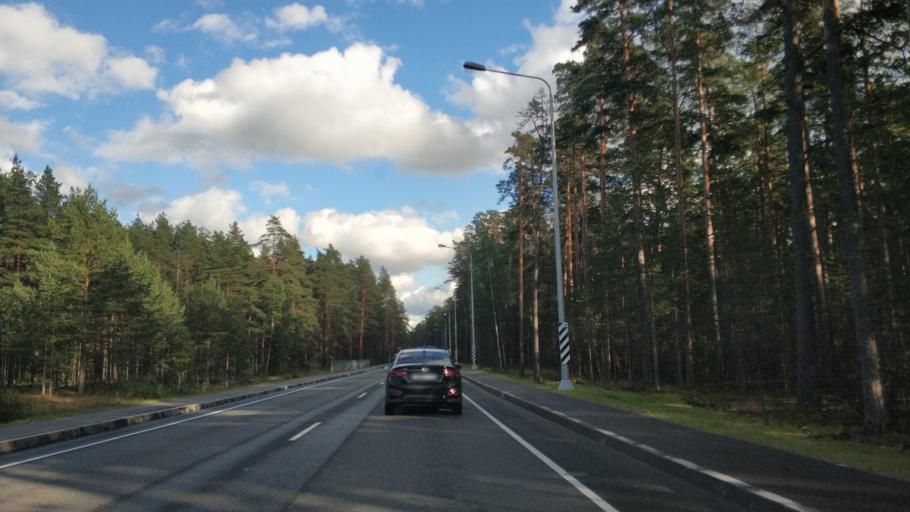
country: RU
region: Leningrad
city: Priozersk
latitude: 61.0127
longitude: 30.1543
